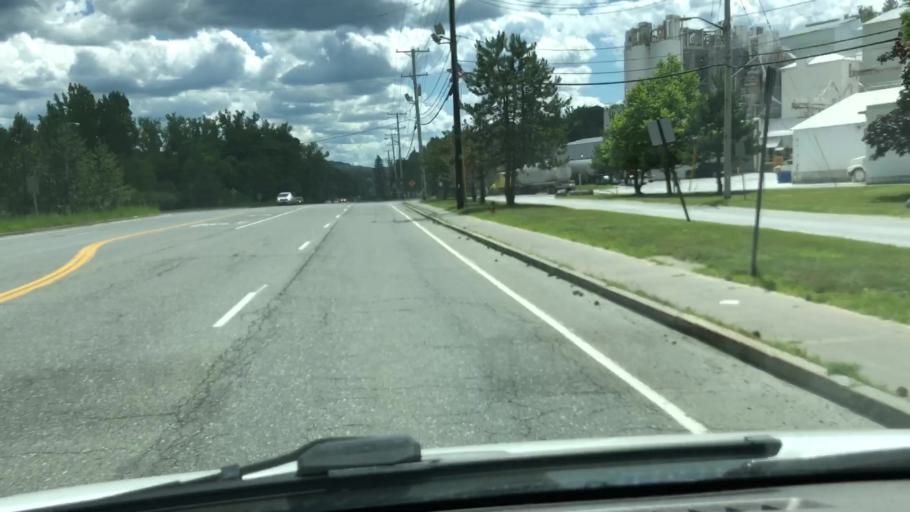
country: US
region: Massachusetts
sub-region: Berkshire County
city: Adams
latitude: 42.6440
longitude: -73.1122
